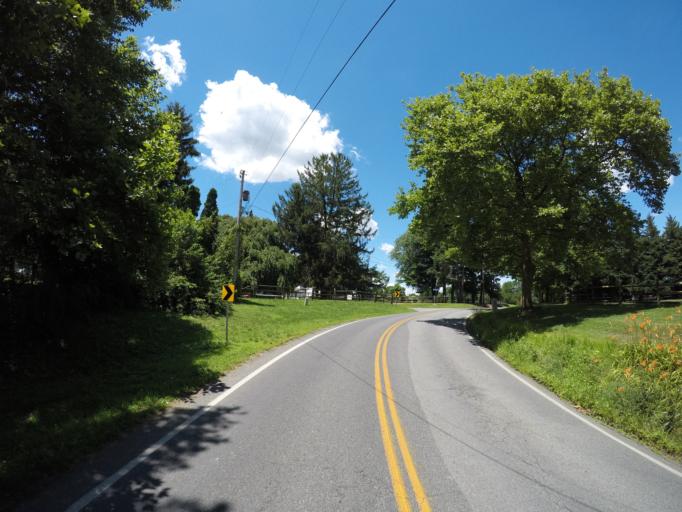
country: US
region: Delaware
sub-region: New Castle County
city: Middletown
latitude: 39.4663
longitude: -75.7788
